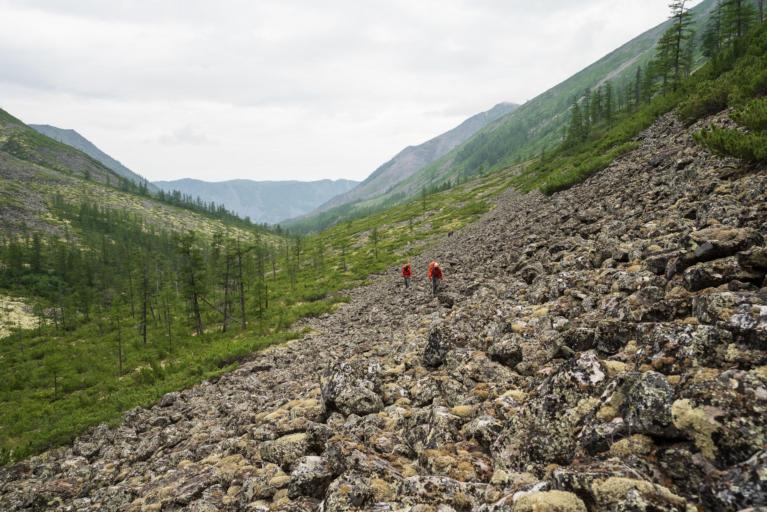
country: RU
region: Transbaikal Territory
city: Kuanda
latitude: 56.6983
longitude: 116.4709
